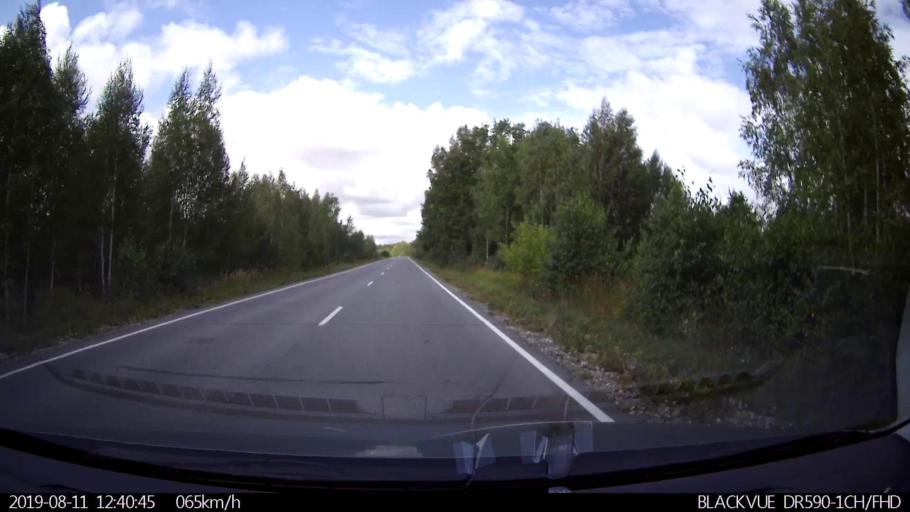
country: RU
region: Ulyanovsk
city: Ignatovka
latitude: 53.8405
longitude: 47.7762
